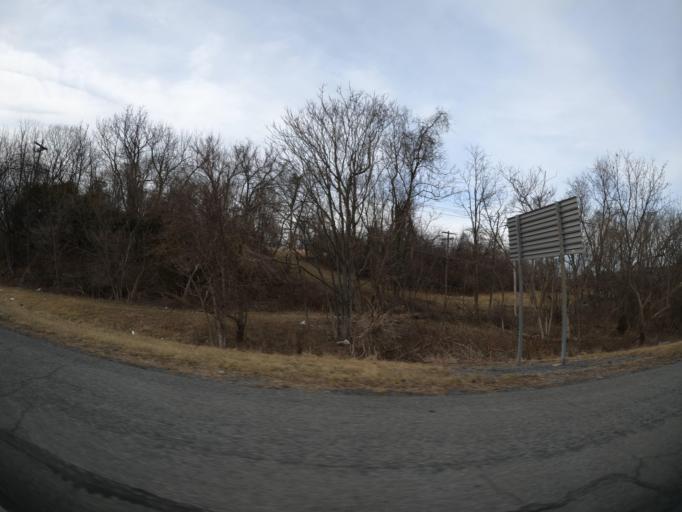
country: US
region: West Virginia
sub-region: Jefferson County
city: Bolivar
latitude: 39.3188
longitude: -77.7650
